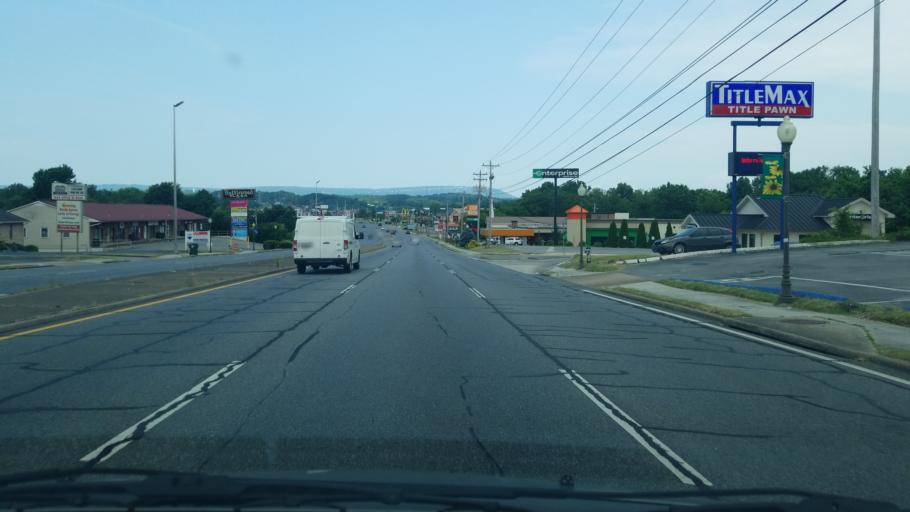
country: US
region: Georgia
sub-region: Catoosa County
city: Fort Oglethorpe
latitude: 34.9506
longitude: -85.2400
